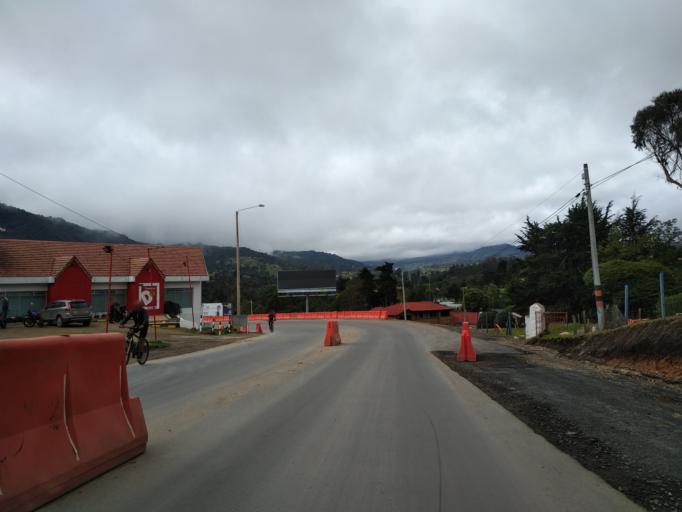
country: CO
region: Bogota D.C.
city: Barrio San Luis
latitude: 4.6611
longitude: -74.0071
